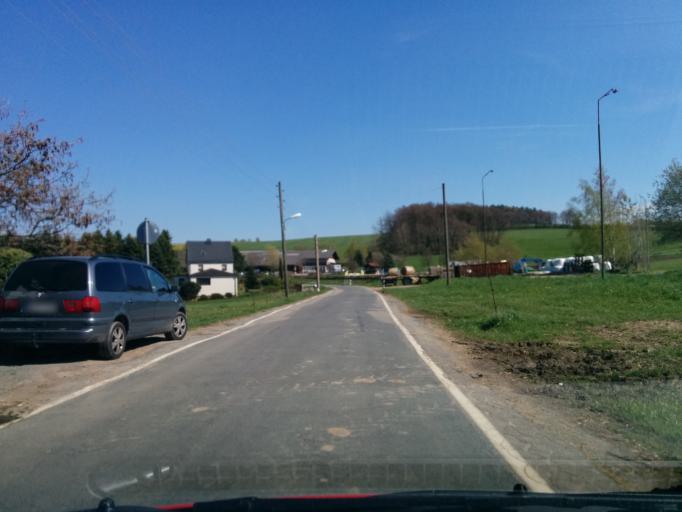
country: DE
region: Saxony
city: Niederwiesa
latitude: 50.8350
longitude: 13.0275
